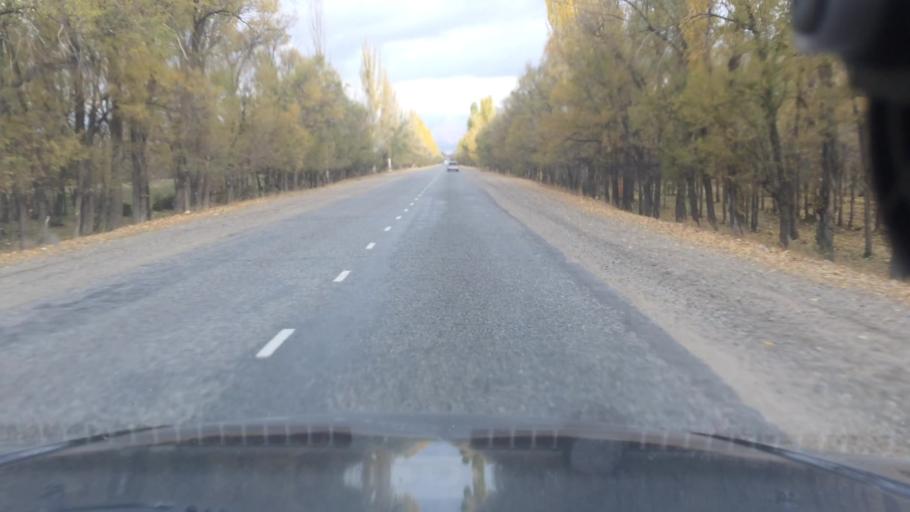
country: KG
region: Ysyk-Koel
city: Tyup
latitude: 42.6322
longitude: 78.3601
